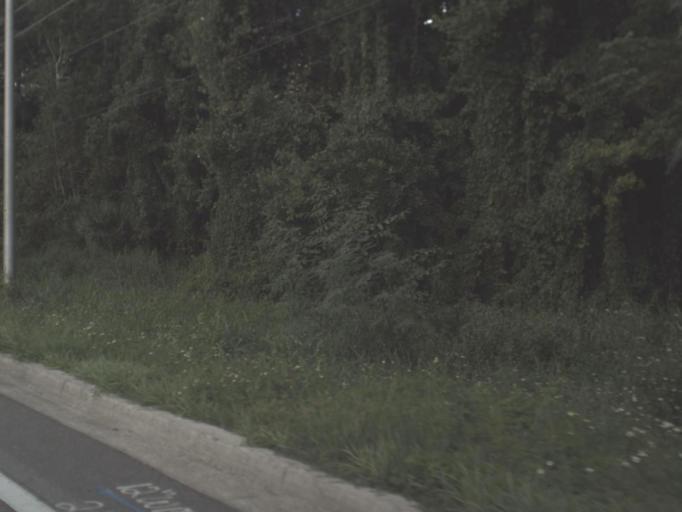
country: US
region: Florida
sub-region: Polk County
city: Loughman
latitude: 28.2346
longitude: -81.5605
